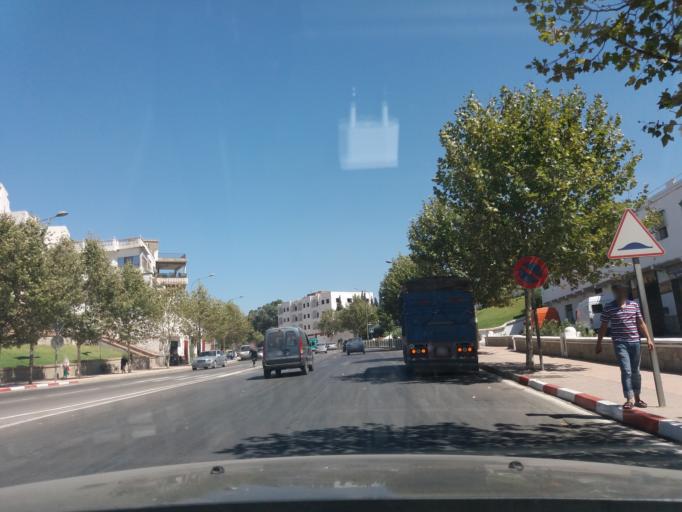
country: MA
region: Tanger-Tetouan
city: Tetouan
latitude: 35.5653
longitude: -5.3978
